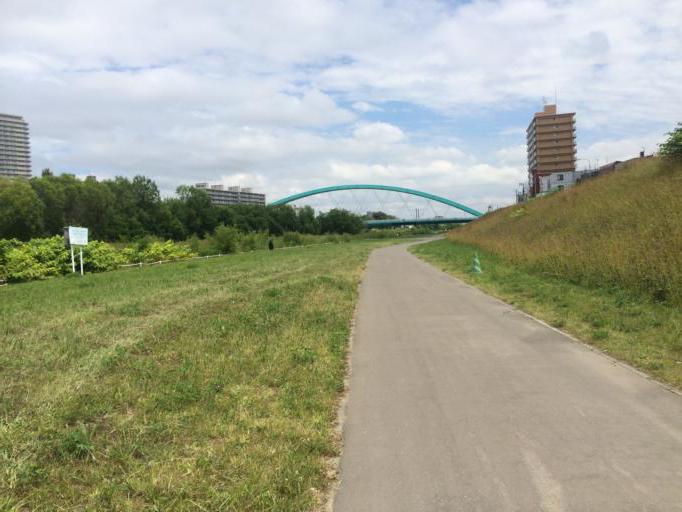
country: JP
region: Hokkaido
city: Sapporo
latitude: 43.0615
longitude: 141.3706
